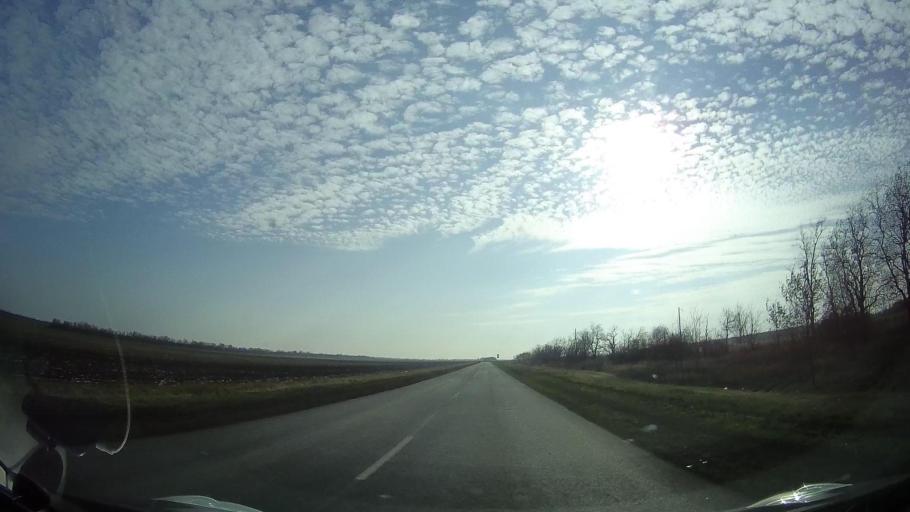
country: RU
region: Rostov
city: Veselyy
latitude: 46.9734
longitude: 40.7196
